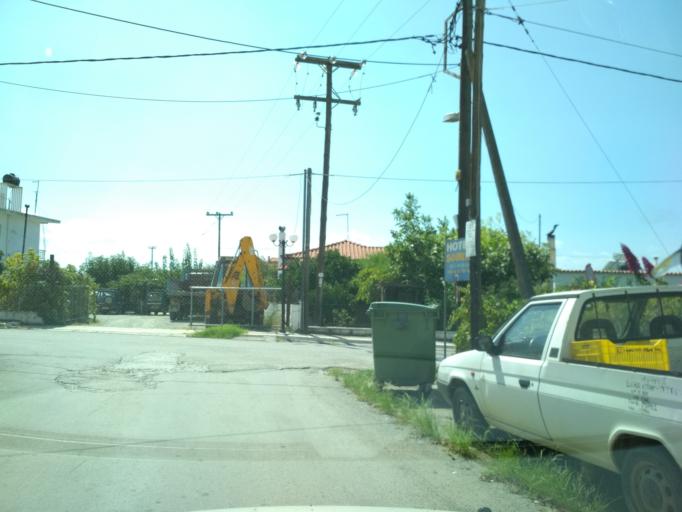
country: GR
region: Central Greece
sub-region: Nomos Evvoias
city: Roviai
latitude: 38.8120
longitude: 23.2280
